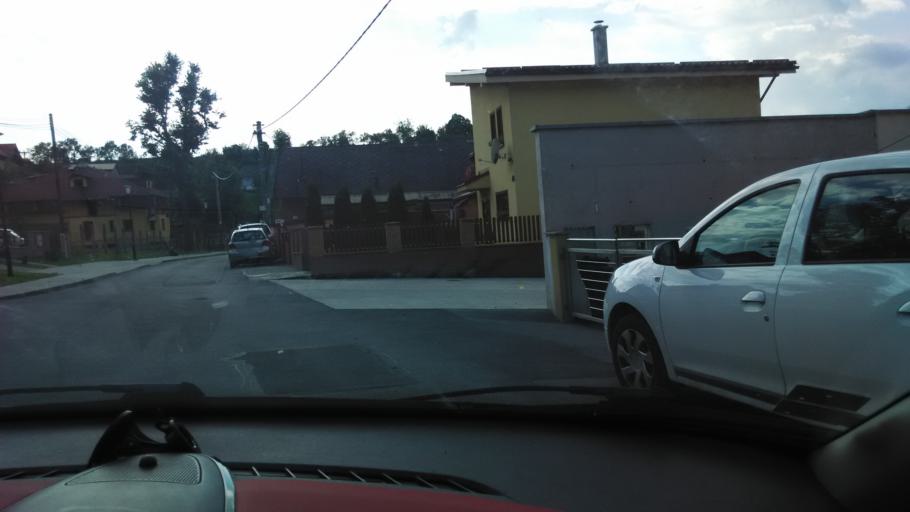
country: SK
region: Zilinsky
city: Kysucke Nove Mesto
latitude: 49.2959
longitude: 18.7896
